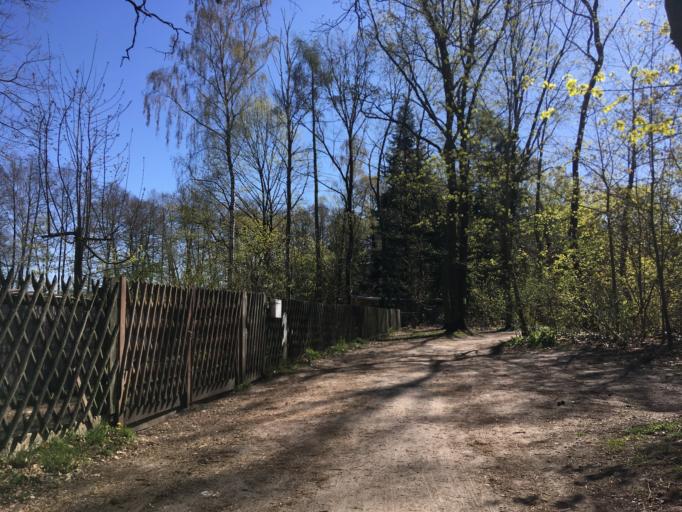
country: DE
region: Brandenburg
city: Wandlitz
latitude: 52.6851
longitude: 13.4673
